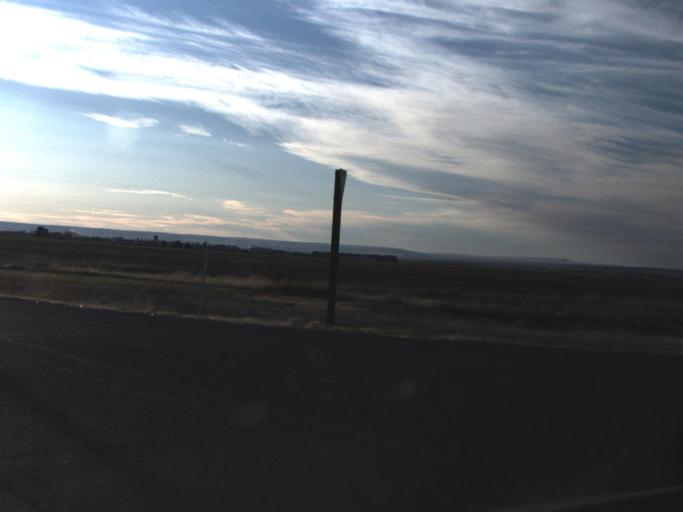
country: US
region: Washington
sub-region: Walla Walla County
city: Walla Walla East
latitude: 46.0992
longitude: -118.2531
